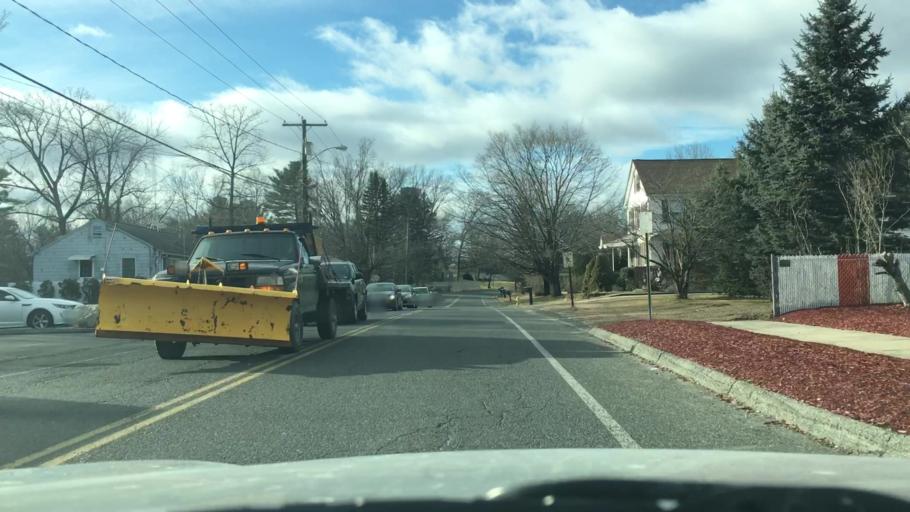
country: US
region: Massachusetts
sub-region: Hampden County
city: Agawam
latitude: 42.0673
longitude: -72.6319
